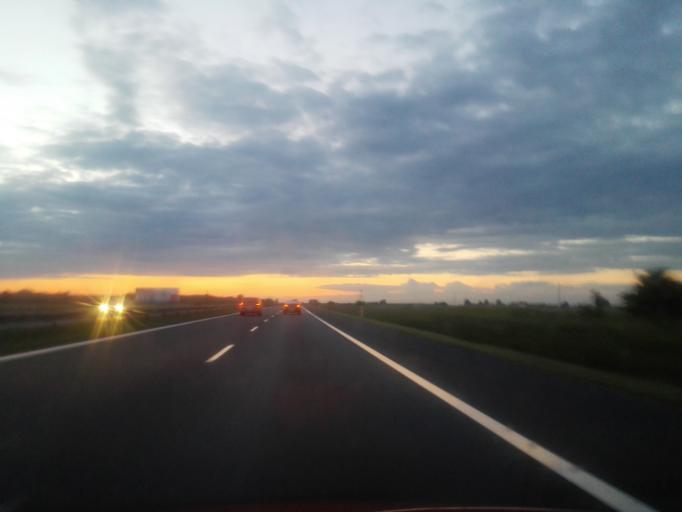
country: PL
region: Lodz Voivodeship
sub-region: Powiat piotrkowski
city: Grabica
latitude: 51.4994
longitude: 19.6075
